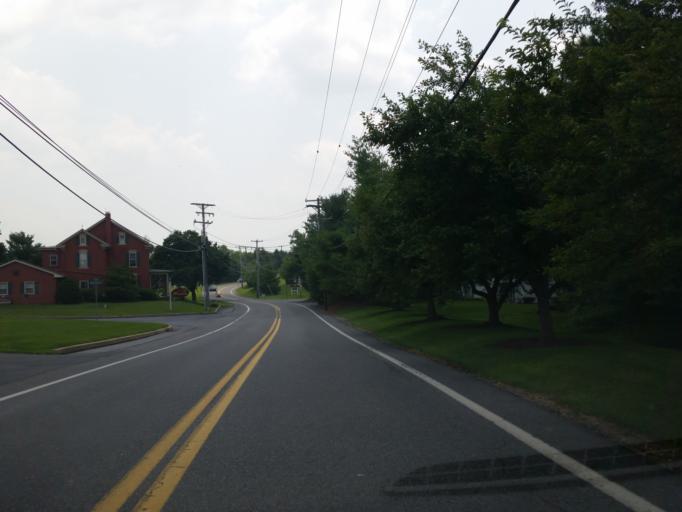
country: US
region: Pennsylvania
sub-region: Dauphin County
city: Palmdale
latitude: 40.2925
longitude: -76.6015
